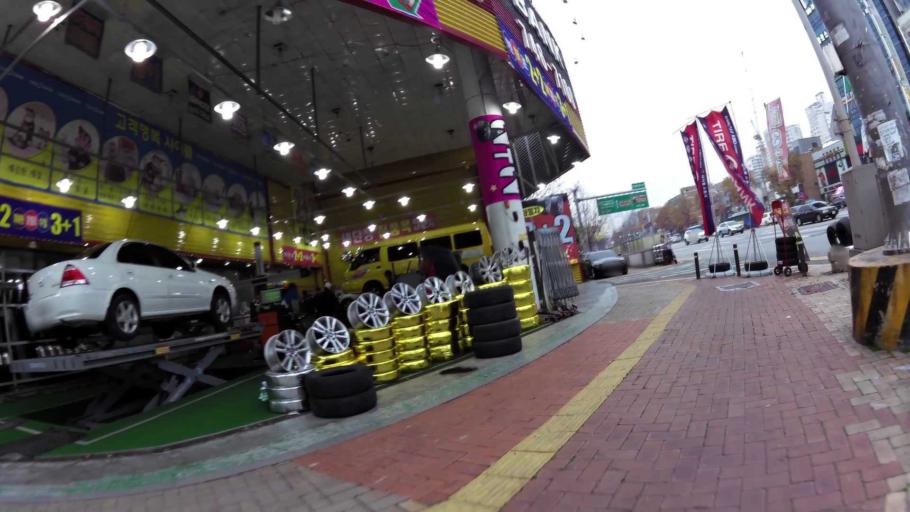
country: KR
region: Daegu
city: Daegu
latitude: 35.8590
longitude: 128.6466
